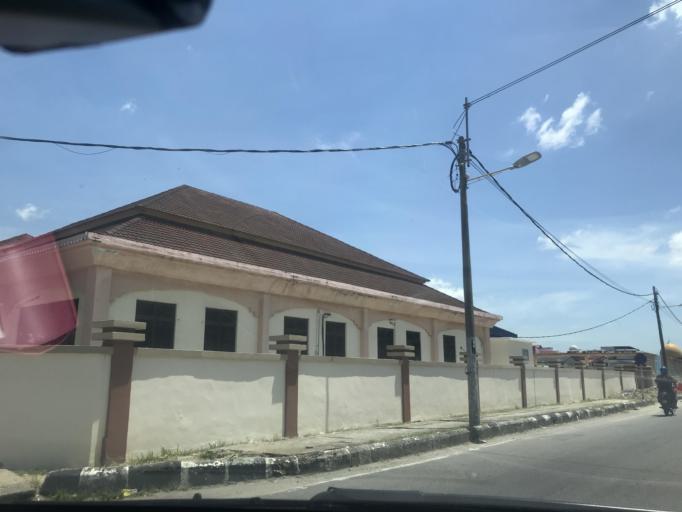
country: MY
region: Kelantan
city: Kota Bharu
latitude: 6.1248
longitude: 102.2472
